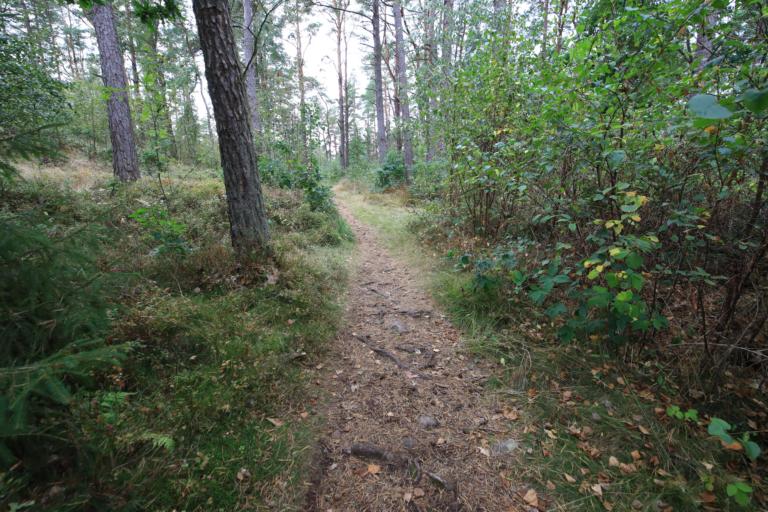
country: SE
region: Halland
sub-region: Varbergs Kommun
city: Varberg
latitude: 57.1749
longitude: 12.2105
